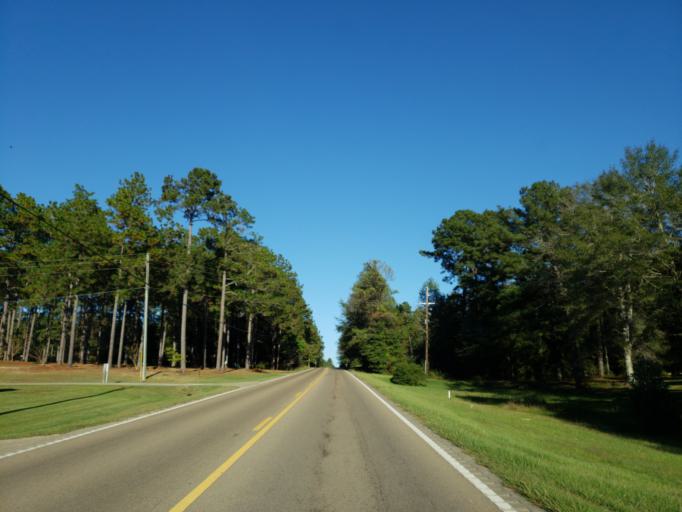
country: US
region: Mississippi
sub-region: Perry County
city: Richton
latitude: 31.3580
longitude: -88.9068
